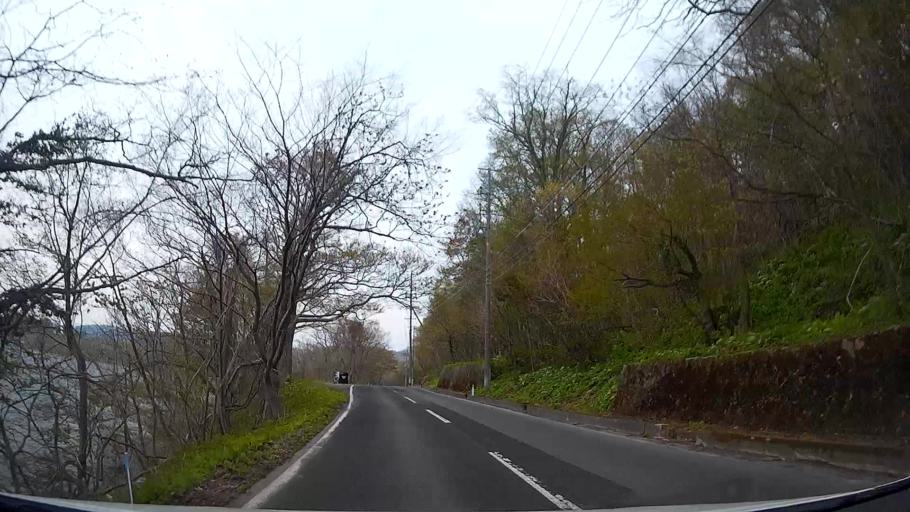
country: JP
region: Akita
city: Hanawa
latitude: 40.4194
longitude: 140.8910
